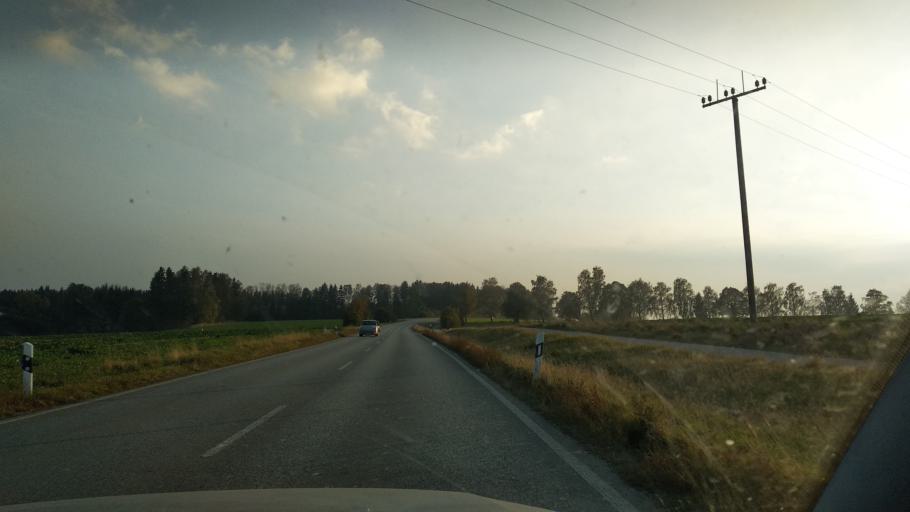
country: DE
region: Bavaria
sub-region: Upper Bavaria
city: Markt Schwaben
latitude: 48.1704
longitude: 11.8625
